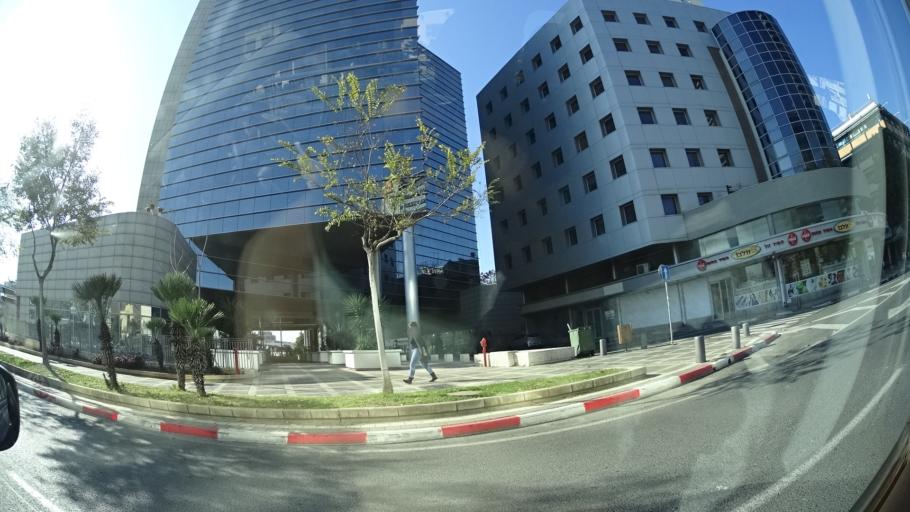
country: IL
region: Tel Aviv
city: Tel Aviv
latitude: 32.0625
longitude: 34.7798
